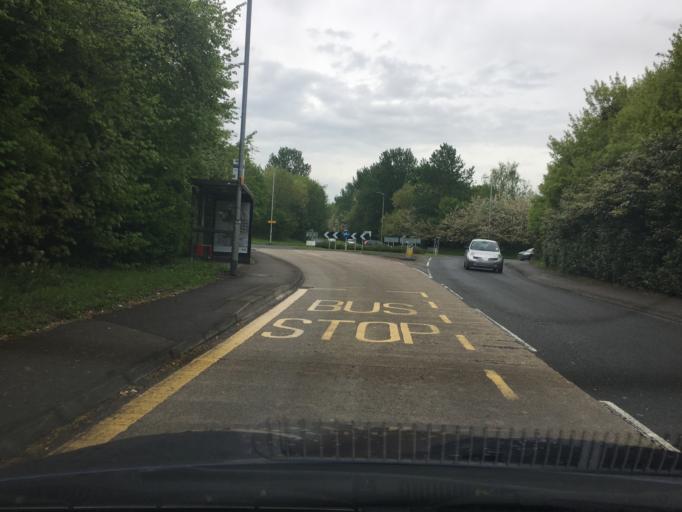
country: GB
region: England
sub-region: Bracknell Forest
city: Sandhurst
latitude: 51.3470
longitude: -0.7848
